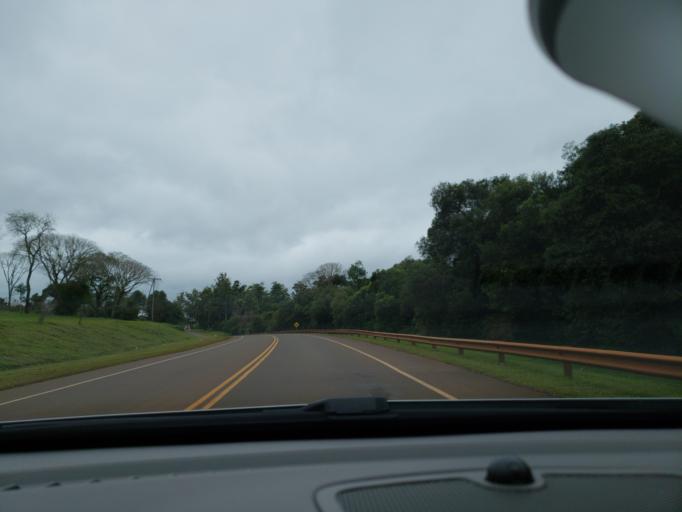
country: AR
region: Misiones
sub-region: Departamento de Apostoles
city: Apostoles
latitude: -27.8725
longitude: -55.7661
